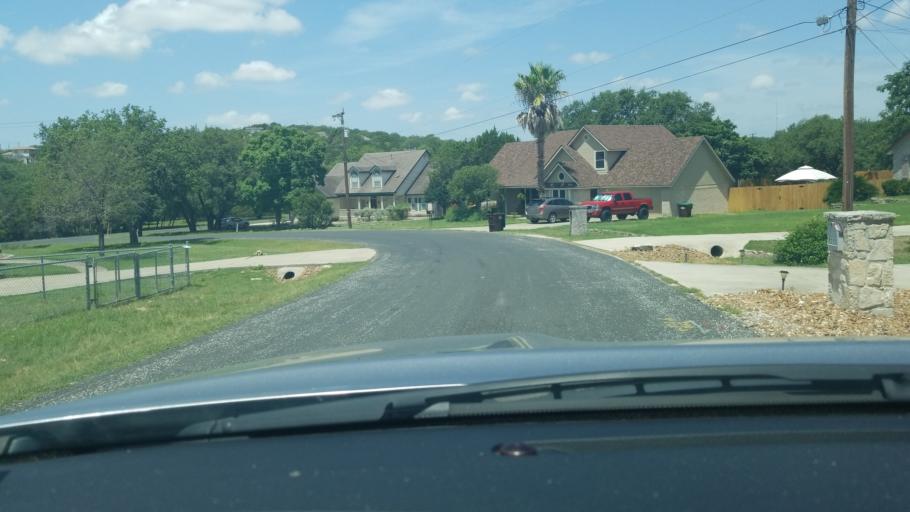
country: US
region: Texas
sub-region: Bexar County
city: Timberwood Park
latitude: 29.6883
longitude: -98.4868
